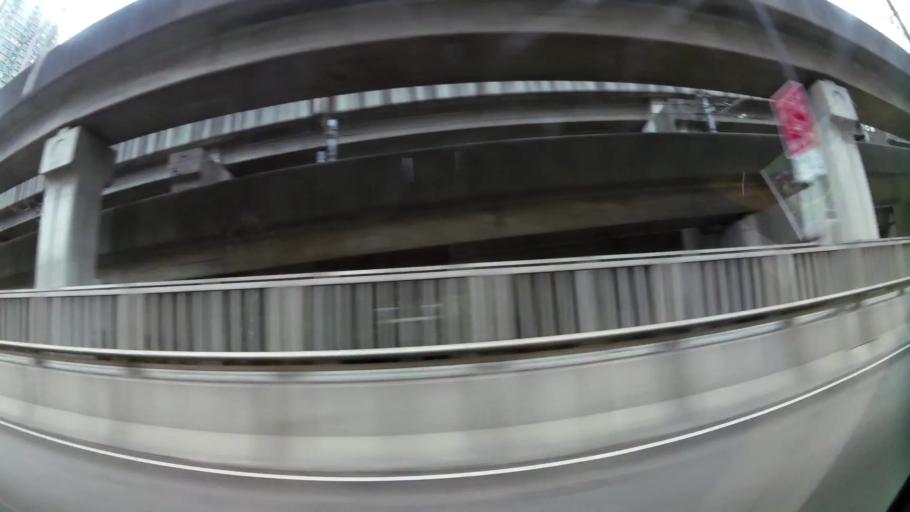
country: HK
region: Tsuen Wan
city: Tsuen Wan
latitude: 22.3592
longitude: 114.1046
